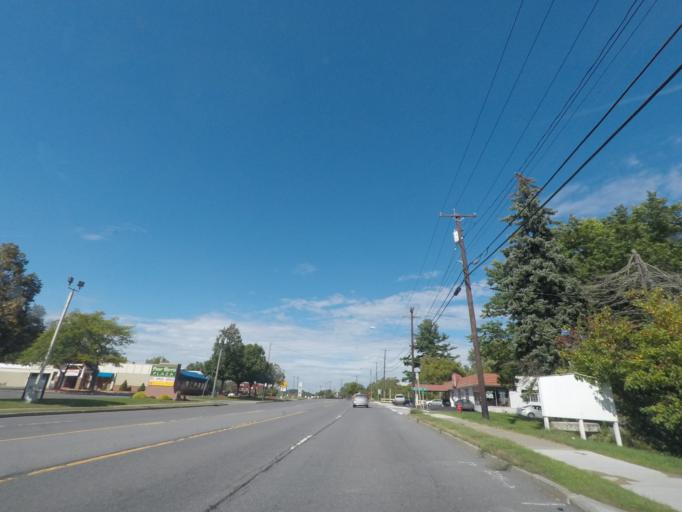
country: US
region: New York
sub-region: Rensselaer County
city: East Greenbush
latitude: 42.6018
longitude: -73.7130
